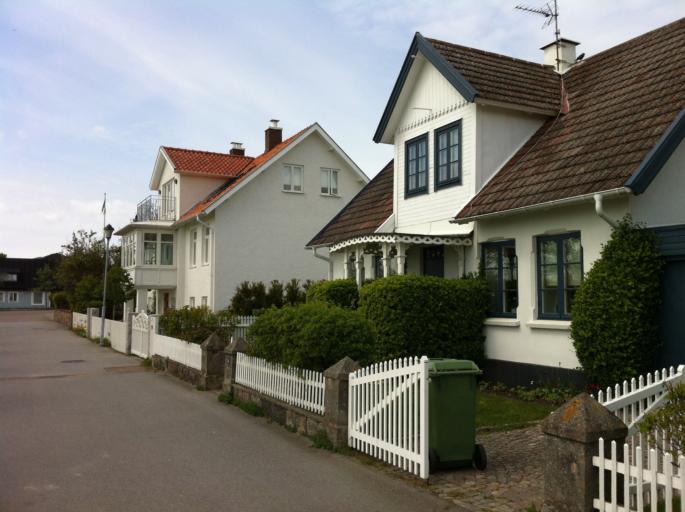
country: SE
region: Skane
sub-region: Hoganas Kommun
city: Hoganas
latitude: 56.1431
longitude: 12.5787
